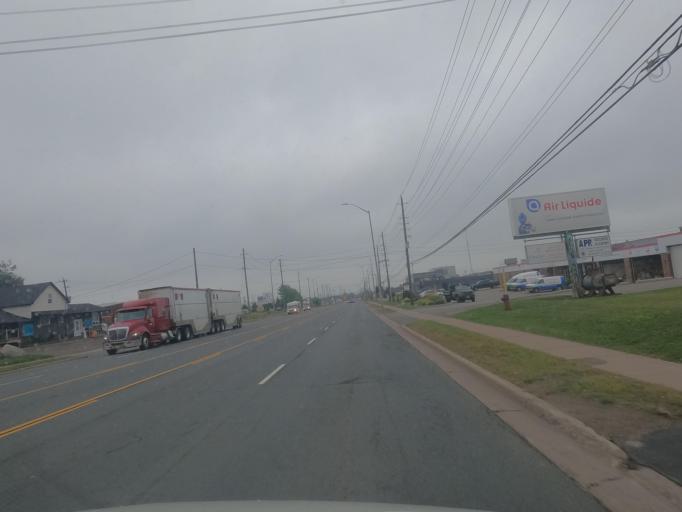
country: CA
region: Ontario
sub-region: Algoma
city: Sault Ste. Marie
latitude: 46.5385
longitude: -84.3226
